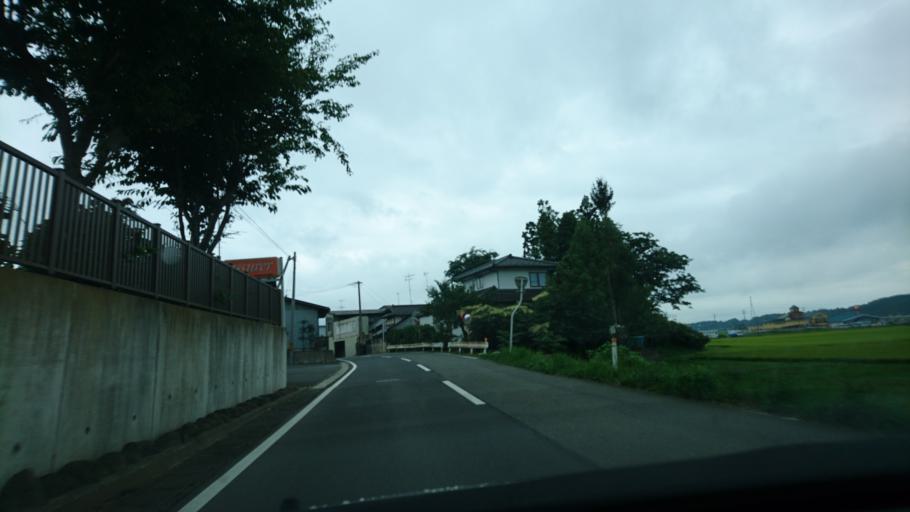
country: JP
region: Iwate
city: Ichinoseki
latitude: 38.8097
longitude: 140.9811
